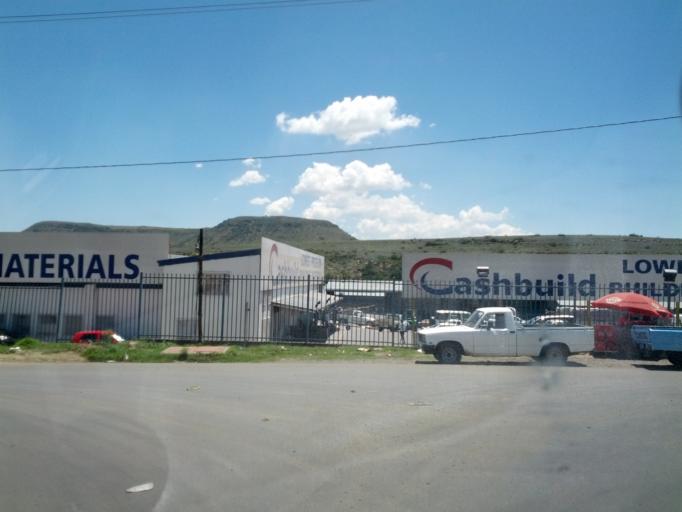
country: LS
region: Maseru
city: Maseru
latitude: -29.2976
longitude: 27.4766
